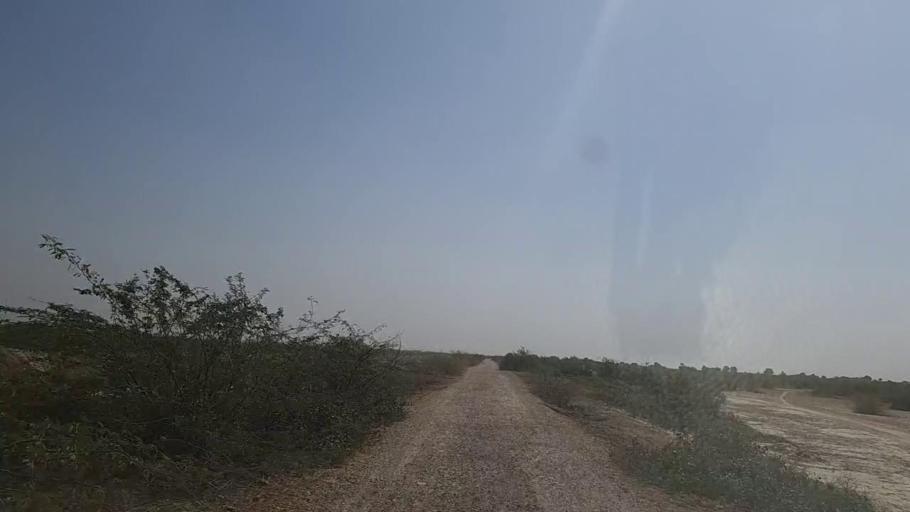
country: PK
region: Sindh
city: Naukot
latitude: 24.6365
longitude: 69.2732
